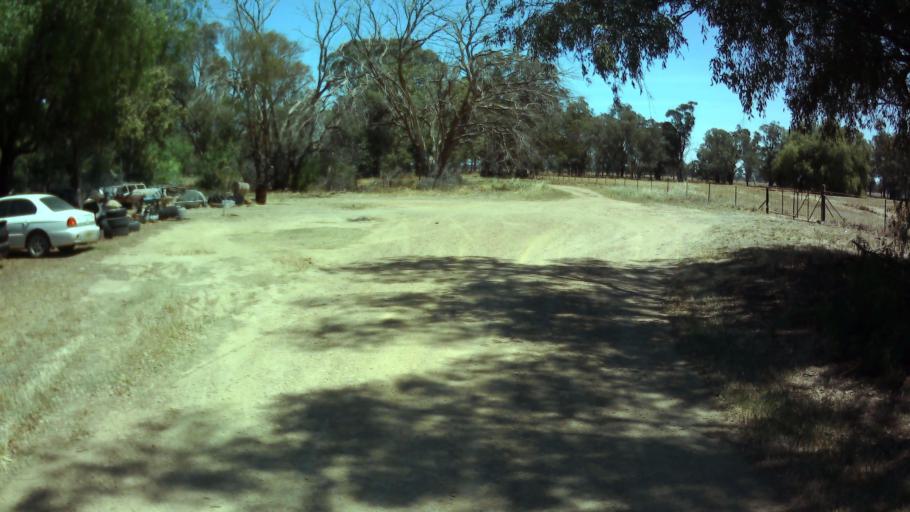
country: AU
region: New South Wales
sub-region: Weddin
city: Grenfell
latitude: -34.0356
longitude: 147.9295
